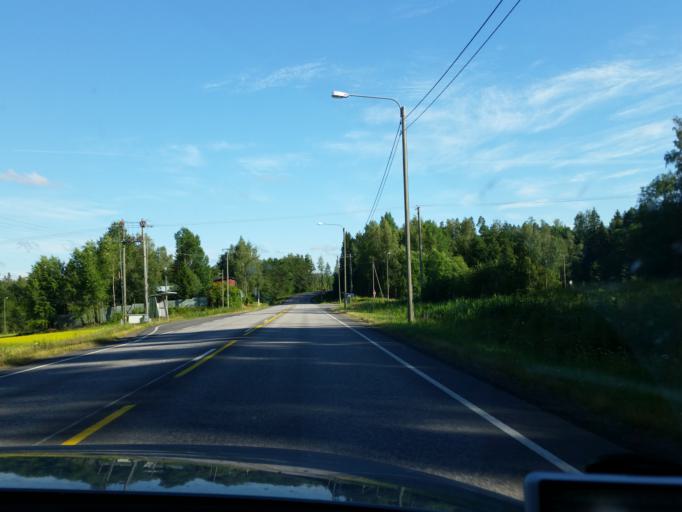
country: FI
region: Uusimaa
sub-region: Helsinki
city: Vihti
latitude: 60.3457
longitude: 24.1928
